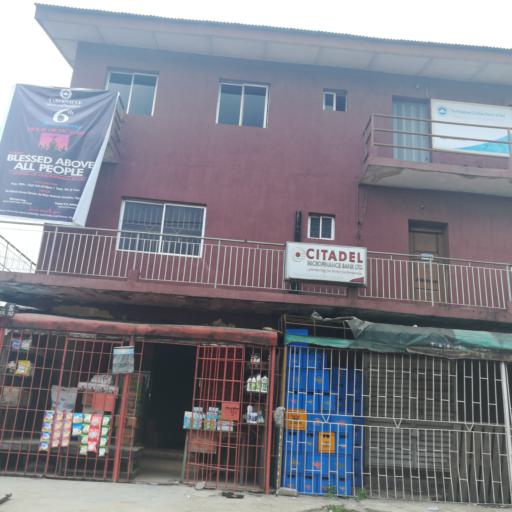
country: NG
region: Lagos
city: Ojota
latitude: 6.5837
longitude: 3.3821
